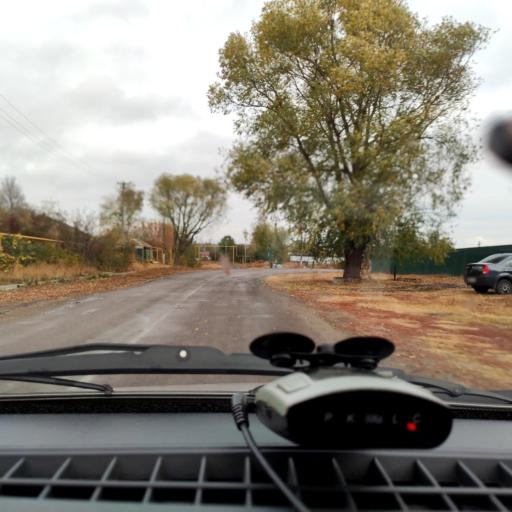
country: RU
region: Voronezj
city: Kolodeznyy
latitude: 51.2388
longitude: 39.0382
